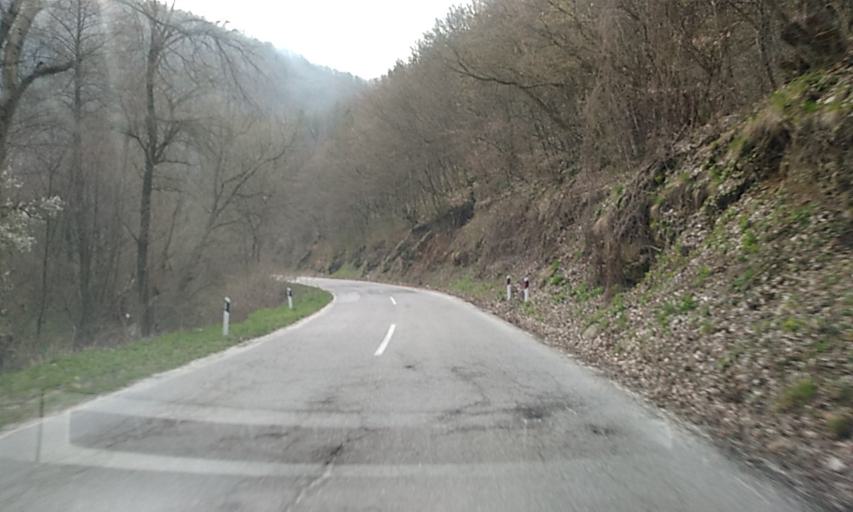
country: RS
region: Central Serbia
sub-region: Pcinjski Okrug
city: Bosilegrad
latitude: 42.5060
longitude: 22.4549
